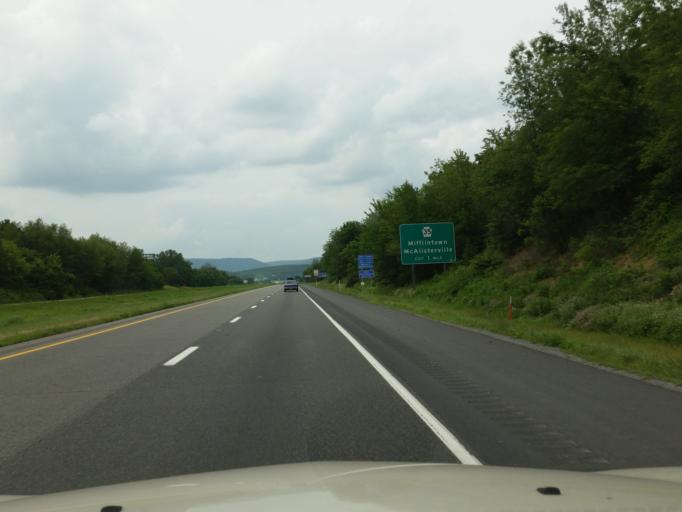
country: US
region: Pennsylvania
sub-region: Juniata County
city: Mifflintown
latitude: 40.5641
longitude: -77.3649
